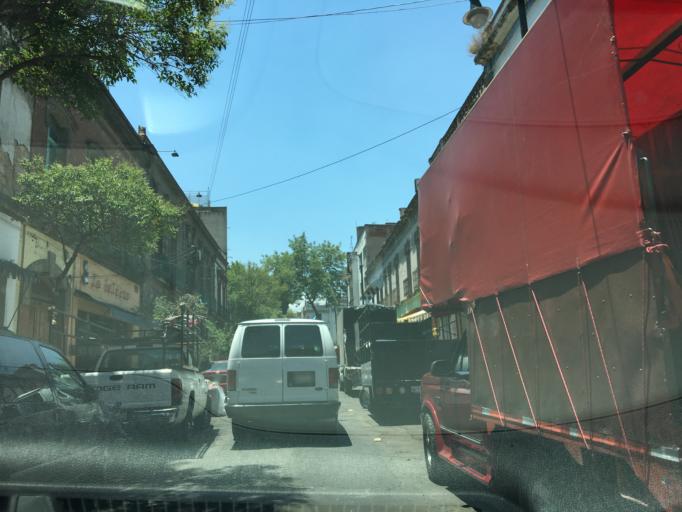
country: MX
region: Mexico City
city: Cuauhtemoc
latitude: 19.4418
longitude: -99.1345
